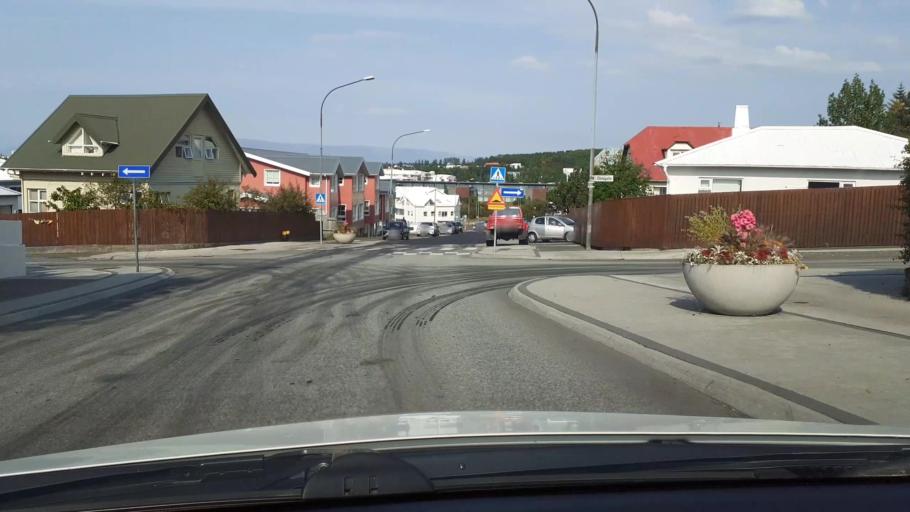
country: IS
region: Capital Region
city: Hafnarfjoerdur
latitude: 64.0652
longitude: -21.9469
